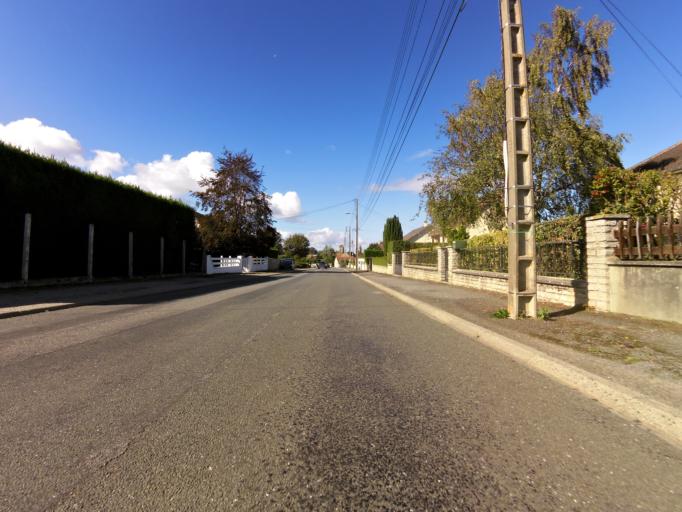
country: FR
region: Lower Normandy
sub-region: Departement du Calvados
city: Saint-Sylvain
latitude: 49.0554
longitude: -0.2115
